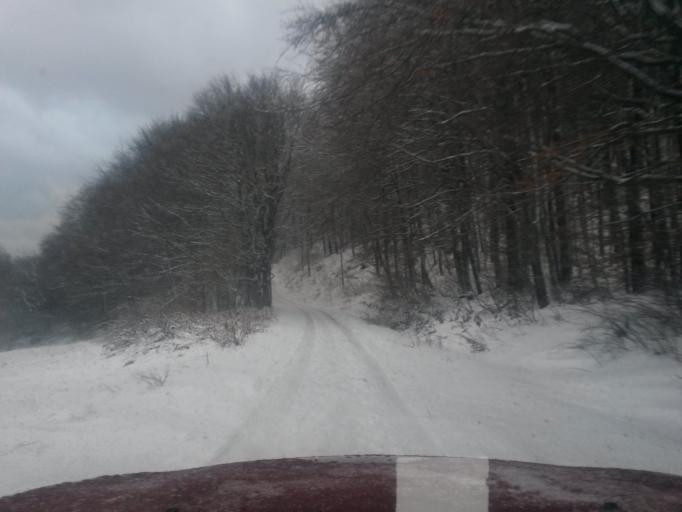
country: SK
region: Kosicky
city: Kosice
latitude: 48.7646
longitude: 21.1311
